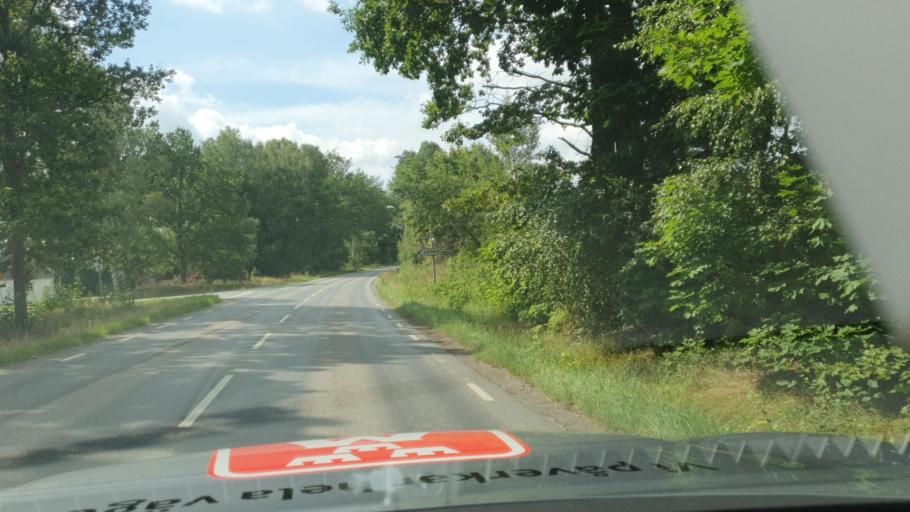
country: SE
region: Skane
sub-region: Ostra Goinge Kommun
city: Knislinge
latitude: 56.1889
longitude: 14.0739
